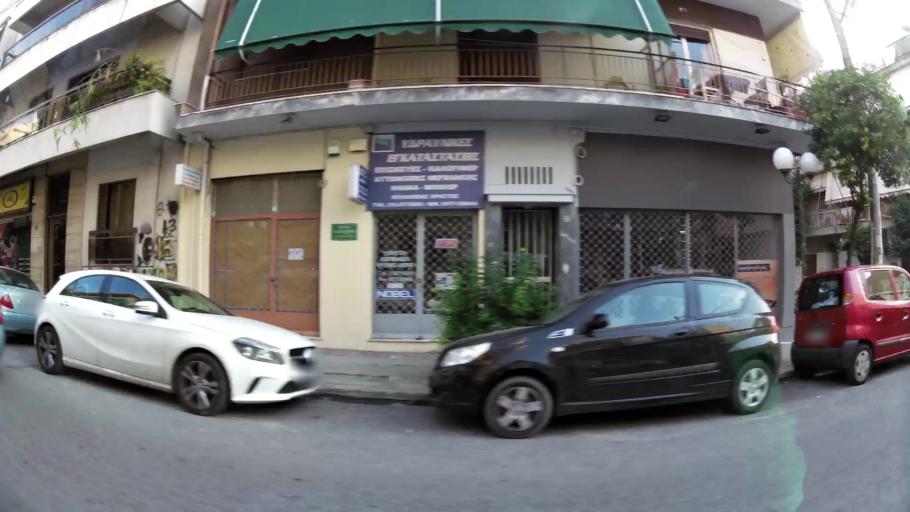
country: GR
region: Attica
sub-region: Nomarchia Athinas
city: Nea Filadelfeia
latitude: 38.0321
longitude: 23.7468
